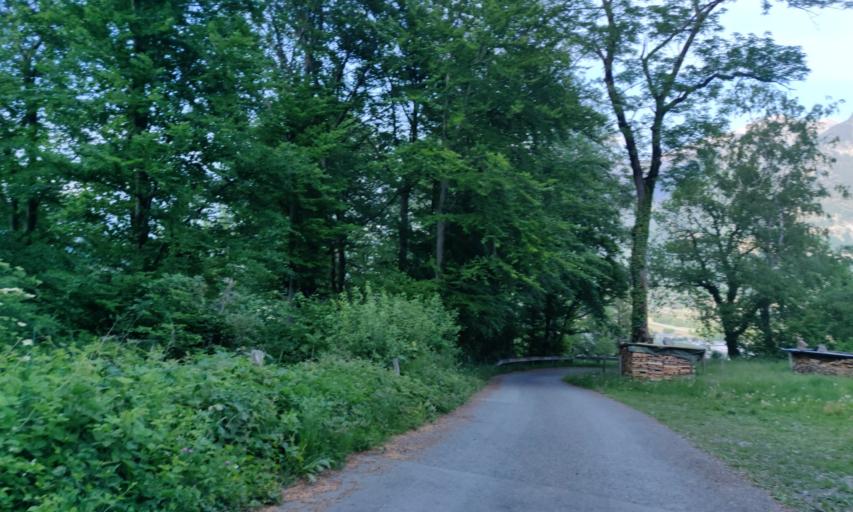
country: LI
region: Balzers
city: Balzers
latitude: 47.0732
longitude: 9.4677
